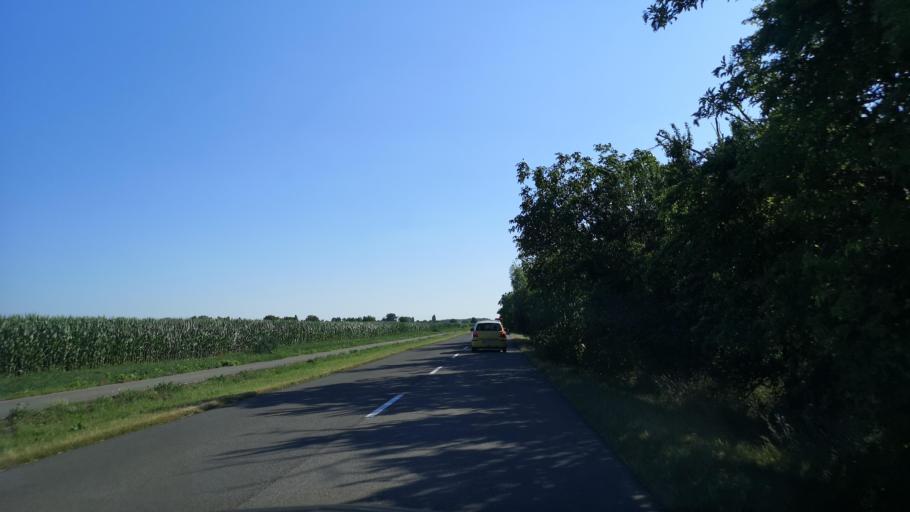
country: SK
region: Trnavsky
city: Dunajska Streda
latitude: 48.0353
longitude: 17.5498
